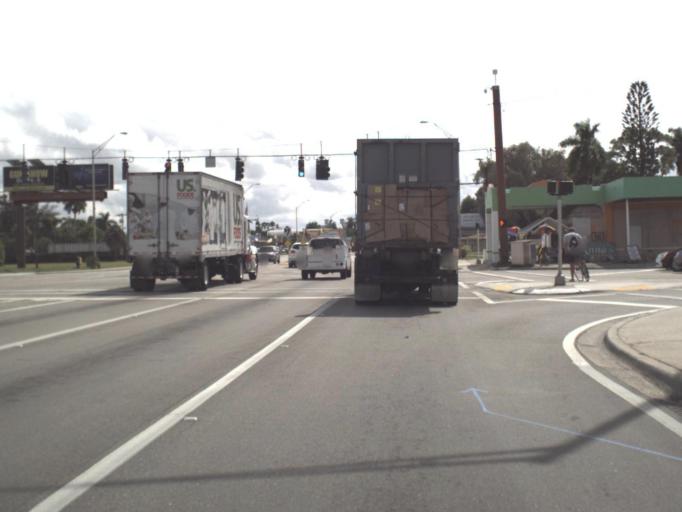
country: US
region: Florida
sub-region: Lee County
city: North Fort Myers
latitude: 26.6678
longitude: -81.8808
